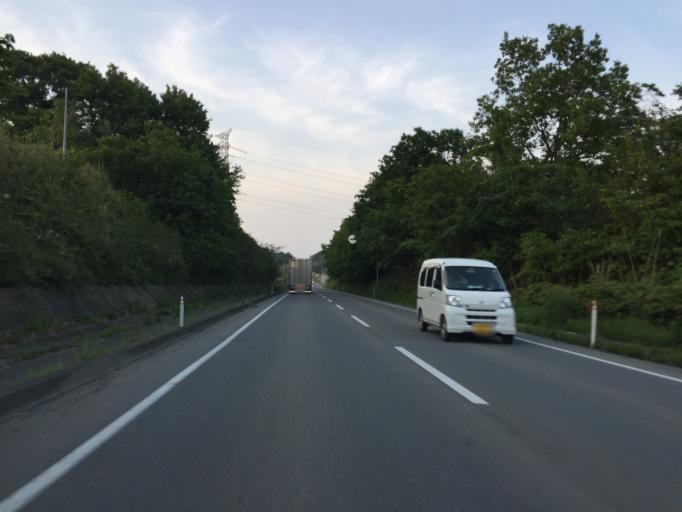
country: JP
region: Fukushima
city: Namie
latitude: 37.4238
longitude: 141.0043
